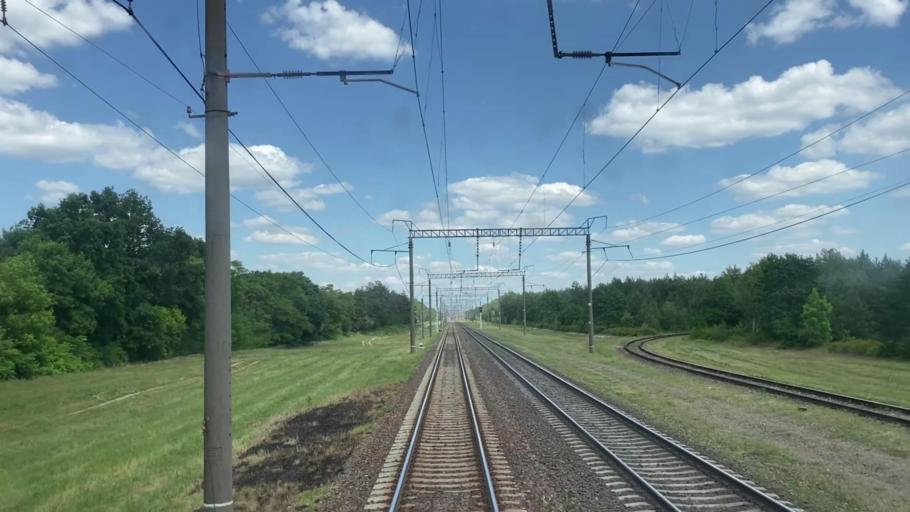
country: BY
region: Brest
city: Brest
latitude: 52.1229
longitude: 23.7840
